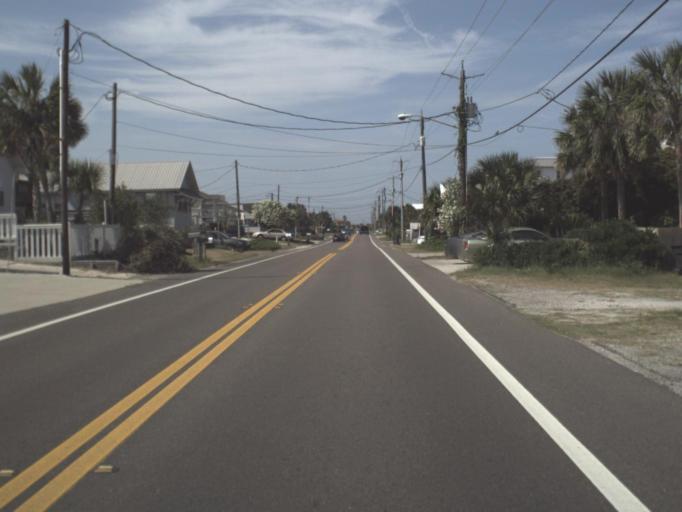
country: US
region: Florida
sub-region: Nassau County
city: Fernandina Beach
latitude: 30.6316
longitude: -81.4386
